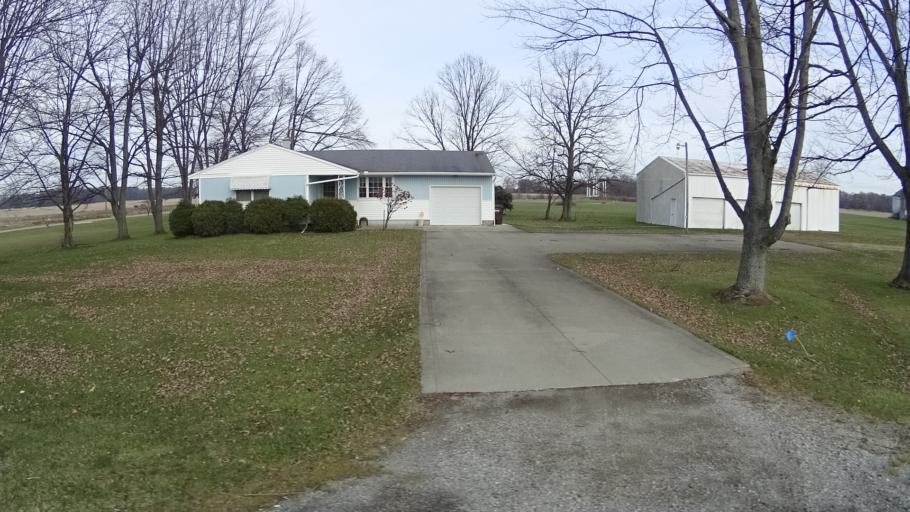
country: US
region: Ohio
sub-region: Lorain County
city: Eaton Estates
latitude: 41.2601
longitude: -82.0019
